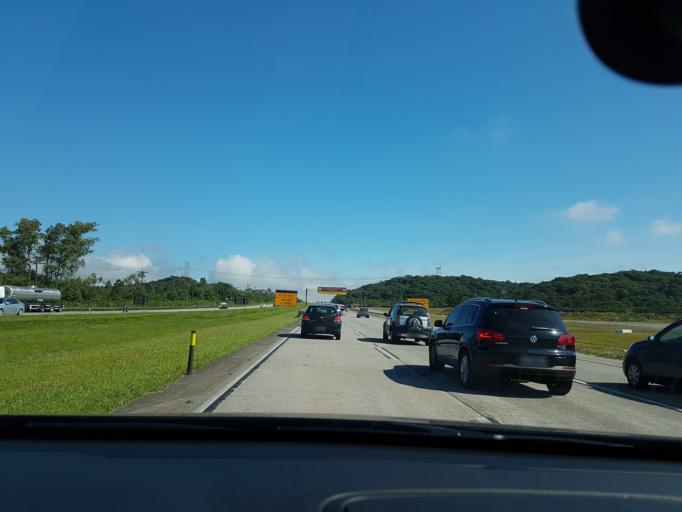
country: BR
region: Sao Paulo
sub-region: Cubatao
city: Cubatao
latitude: -23.8966
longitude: -46.5630
